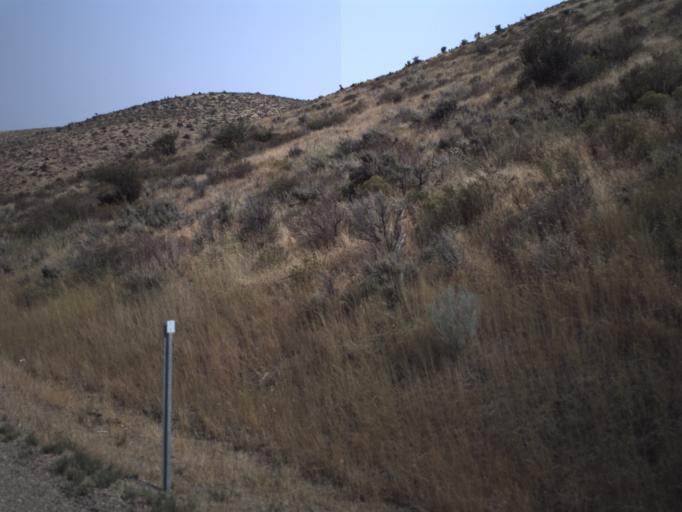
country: US
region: Utah
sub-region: Summit County
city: Summit Park
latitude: 40.8878
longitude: -111.5809
